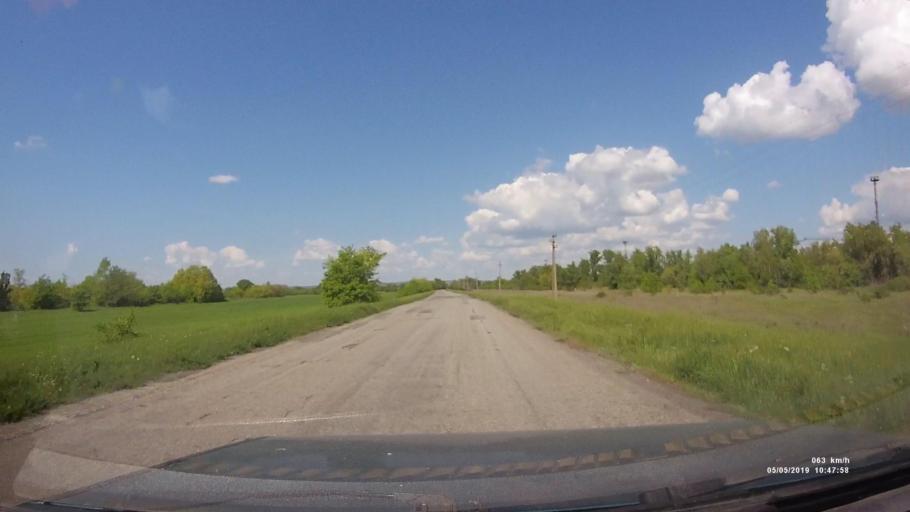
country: RU
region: Rostov
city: Ust'-Donetskiy
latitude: 47.6407
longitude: 40.8258
